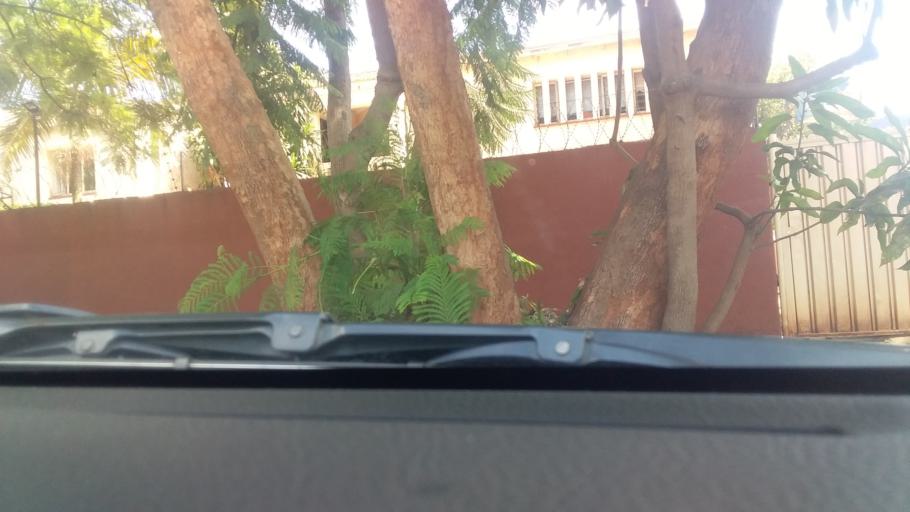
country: ZW
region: Harare
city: Harare
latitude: -17.8197
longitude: 31.0400
